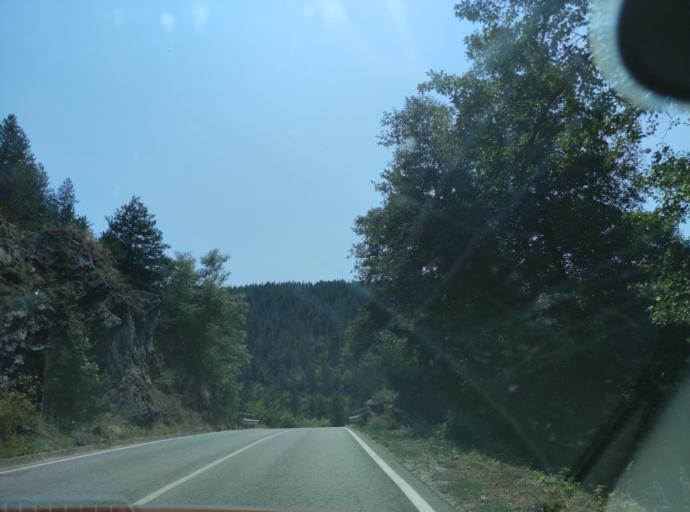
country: BG
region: Blagoevgrad
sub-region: Obshtina Belitsa
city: Belitsa
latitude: 41.8947
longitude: 23.5426
